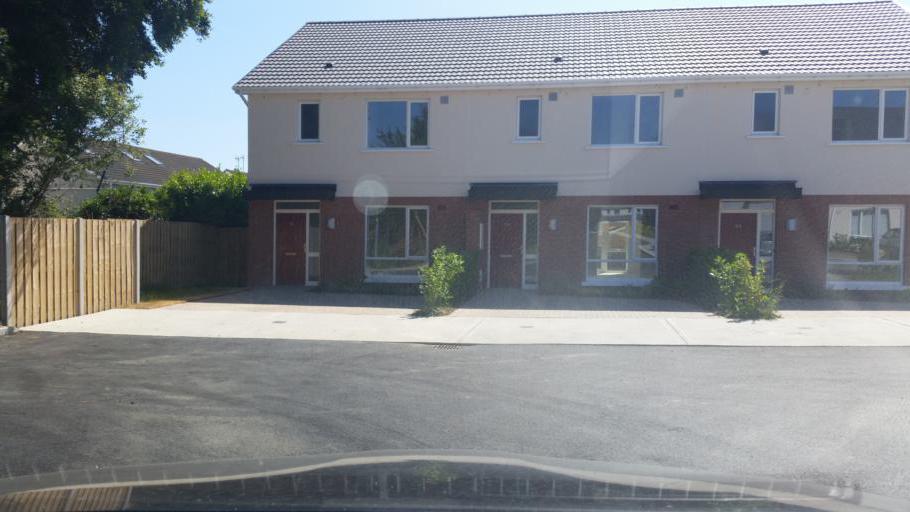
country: IE
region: Leinster
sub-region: Fingal County
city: Swords
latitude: 53.4510
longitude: -6.2501
